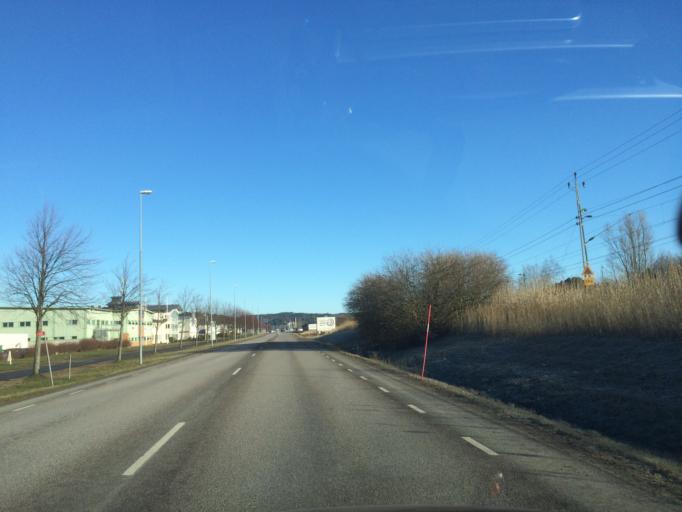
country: SE
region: Halland
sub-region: Kungsbacka Kommun
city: Kungsbacka
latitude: 57.5047
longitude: 12.0805
